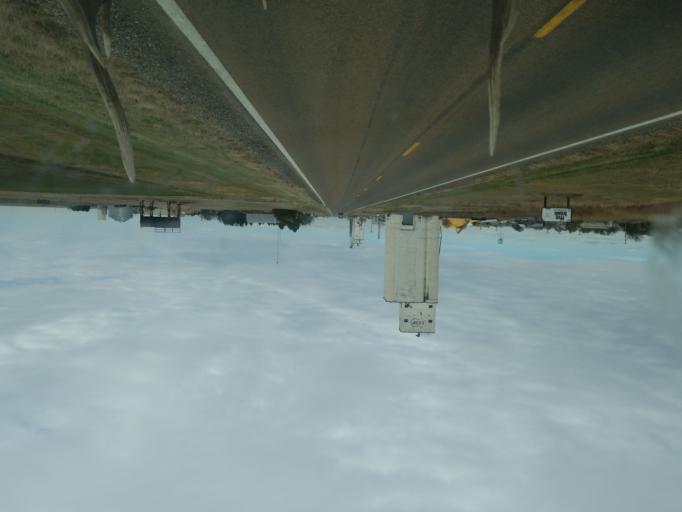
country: US
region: Kansas
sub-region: Thomas County
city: Colby
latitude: 39.0559
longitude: -101.2499
